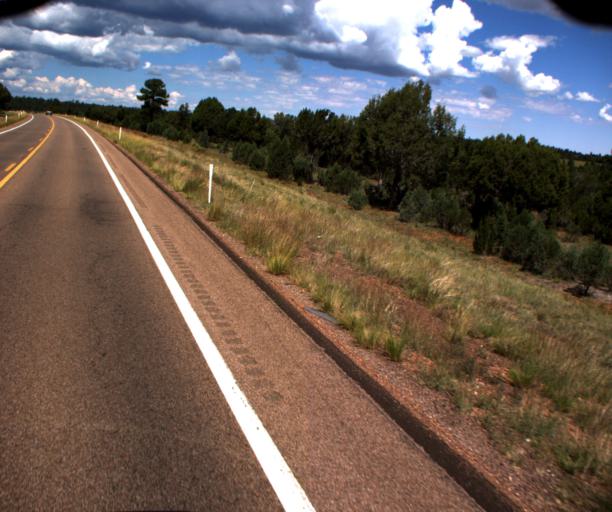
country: US
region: Arizona
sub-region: Navajo County
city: Heber-Overgaard
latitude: 34.3906
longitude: -110.5070
